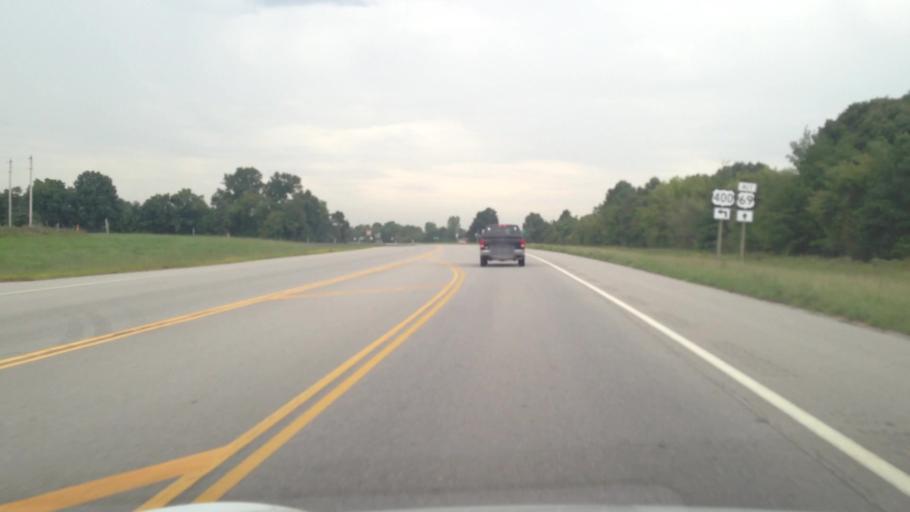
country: US
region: Kansas
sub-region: Cherokee County
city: Baxter Springs
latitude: 37.0574
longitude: -94.7343
